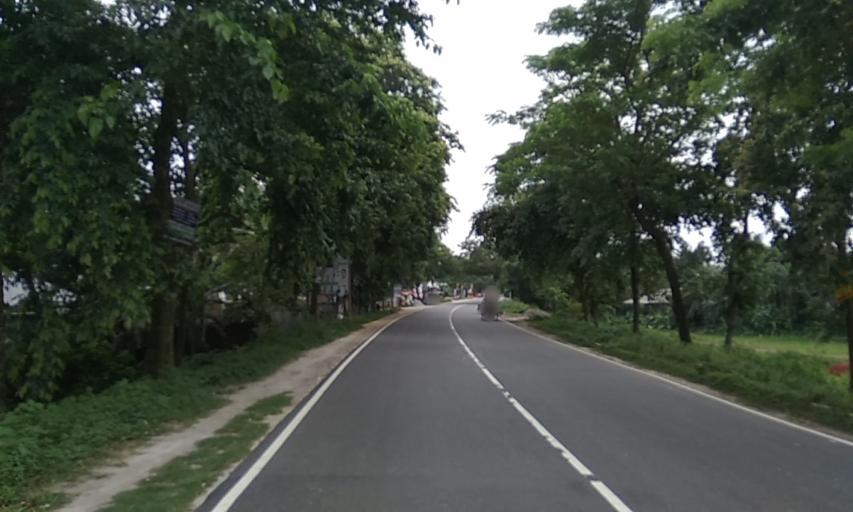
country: BD
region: Rangpur Division
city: Rangpur
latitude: 25.8010
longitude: 89.1887
